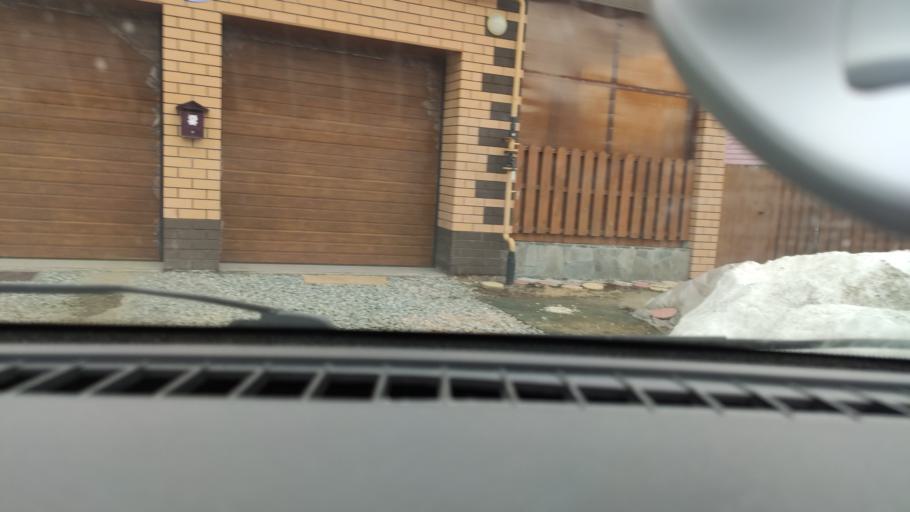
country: RU
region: Perm
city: Perm
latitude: 57.9906
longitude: 56.3098
